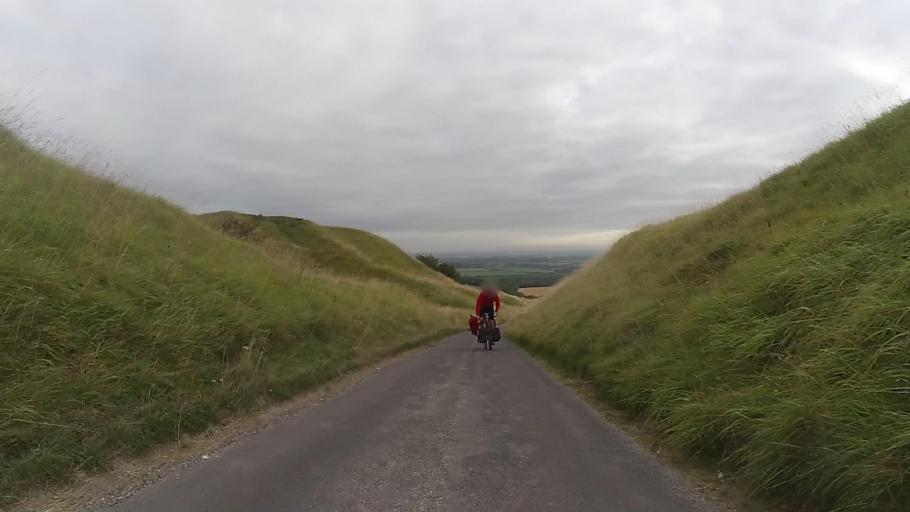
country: GB
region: England
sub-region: West Berkshire
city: Lambourn
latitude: 51.5791
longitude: -1.5671
